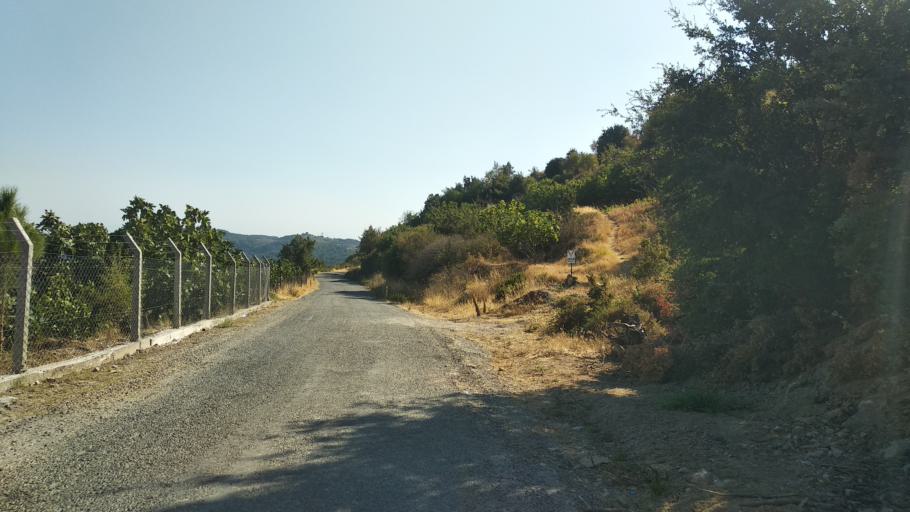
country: TR
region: Izmir
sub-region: Seferihisar
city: Seferhisar
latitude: 38.3205
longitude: 26.9296
